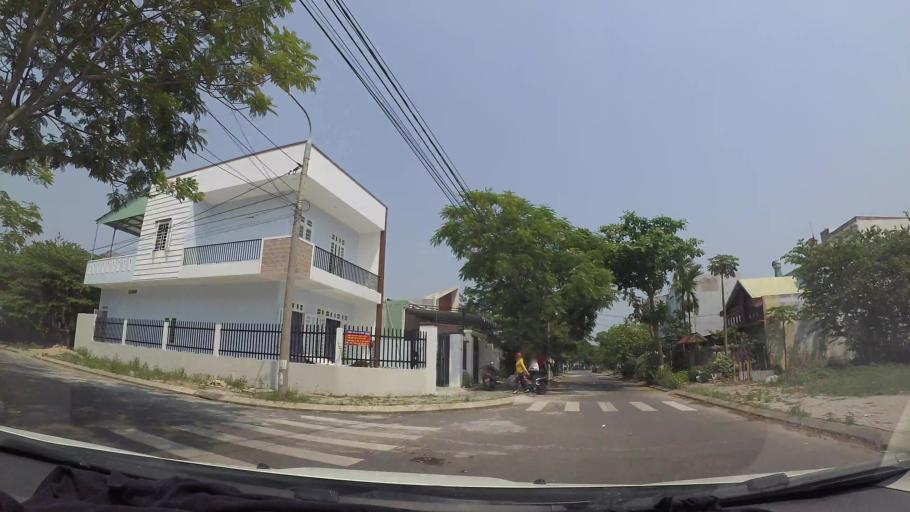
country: VN
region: Da Nang
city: Cam Le
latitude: 15.9925
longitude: 108.2045
